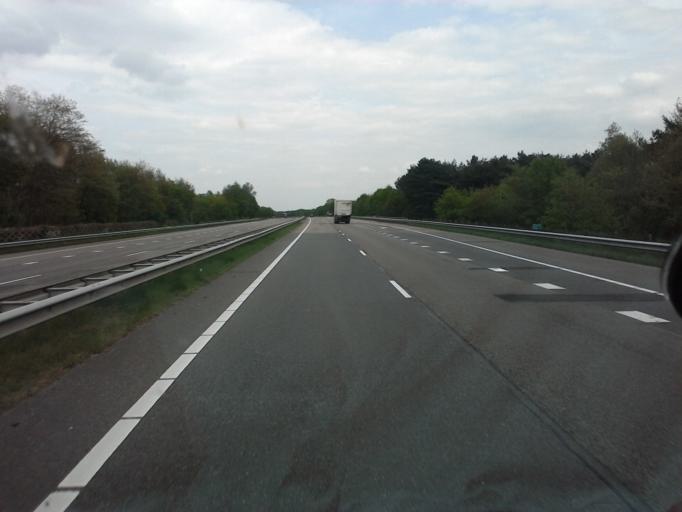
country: NL
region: Limburg
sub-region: Gemeente Gennep
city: Gennep
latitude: 51.6662
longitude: 5.9848
